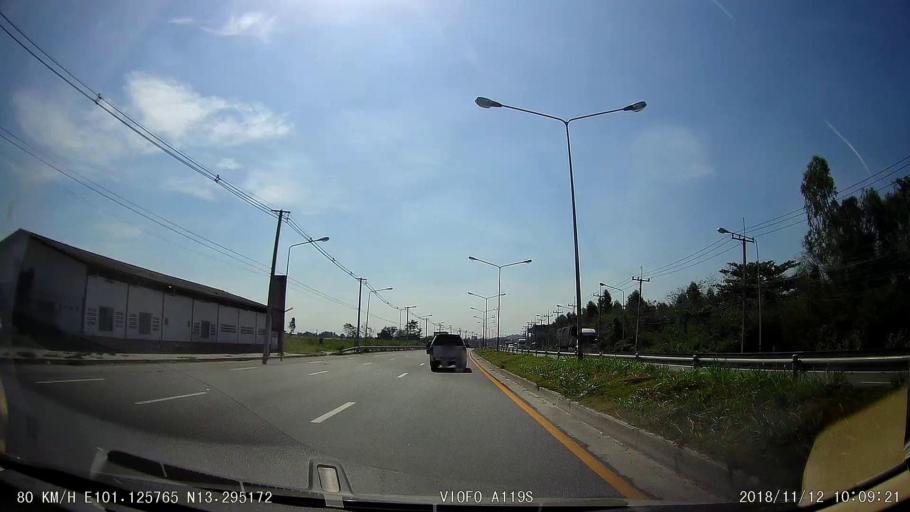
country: TH
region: Chon Buri
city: Ban Bueng
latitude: 13.2950
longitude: 101.1258
